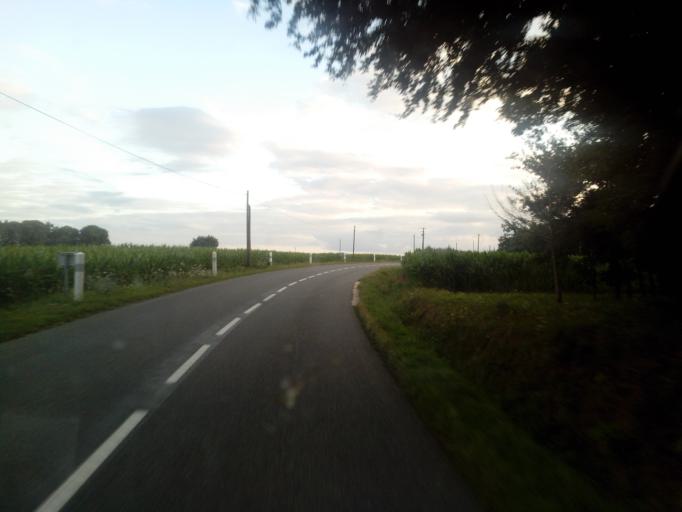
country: FR
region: Brittany
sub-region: Departement du Morbihan
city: Meneac
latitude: 48.1116
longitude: -2.5019
